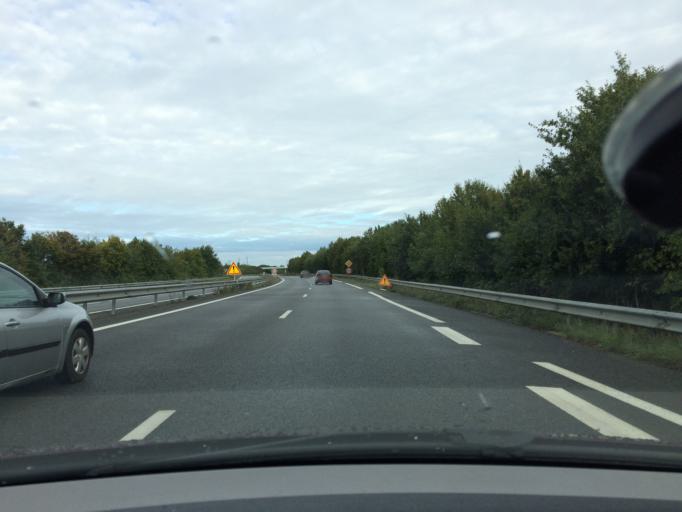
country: FR
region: Brittany
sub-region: Departement d'Ille-et-Vilaine
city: Janze
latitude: 47.9545
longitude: -1.5121
